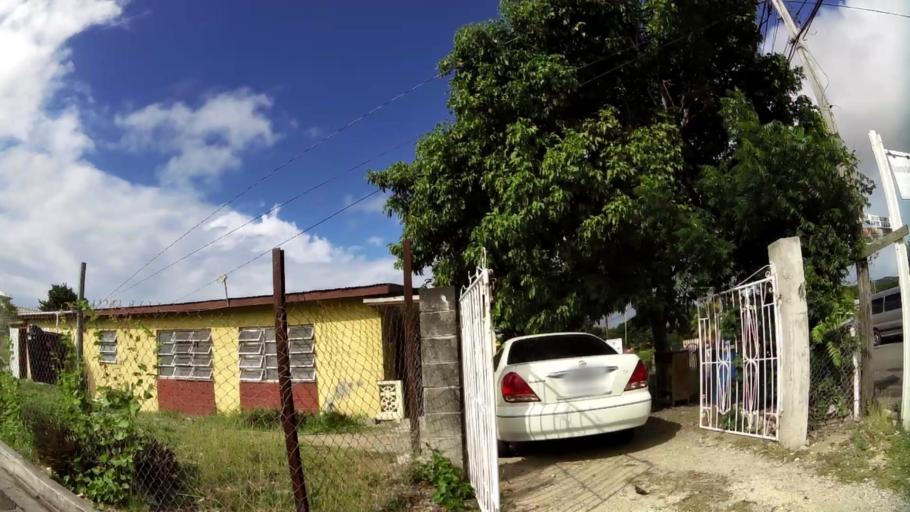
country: AG
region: Saint John
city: Saint John's
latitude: 17.1200
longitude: -61.8282
